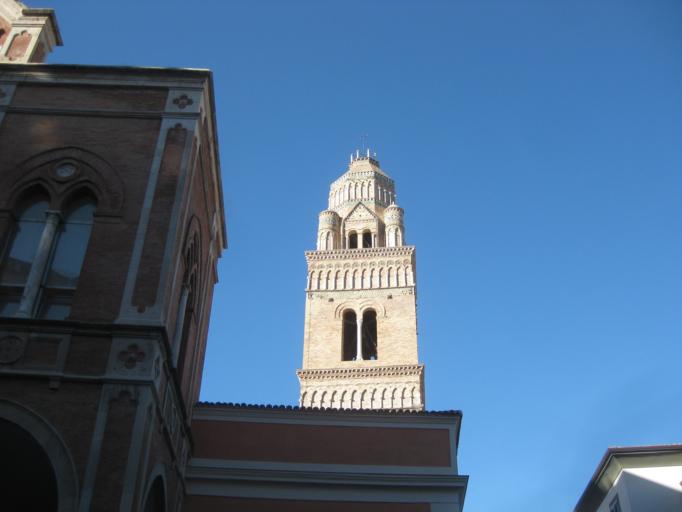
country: IT
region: Latium
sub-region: Provincia di Latina
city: Gaeta
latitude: 41.2086
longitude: 13.5869
